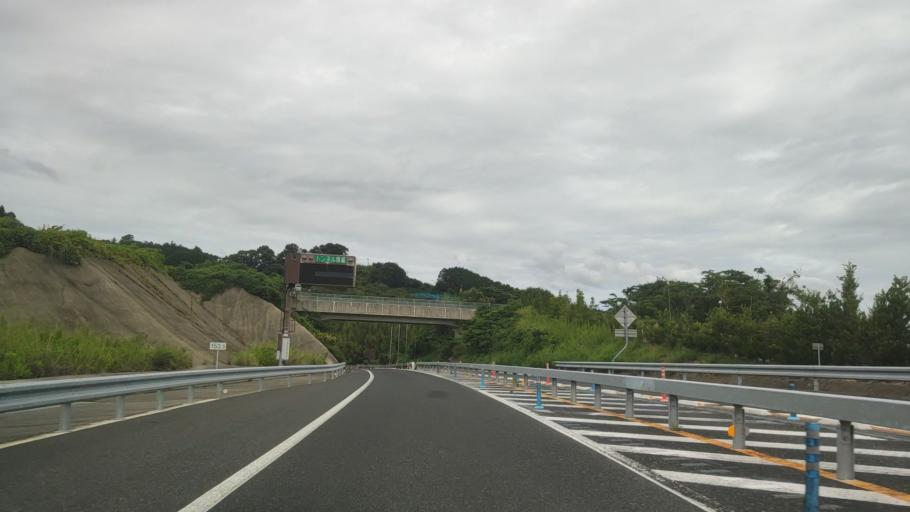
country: JP
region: Wakayama
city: Tanabe
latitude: 33.7657
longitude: 135.3512
